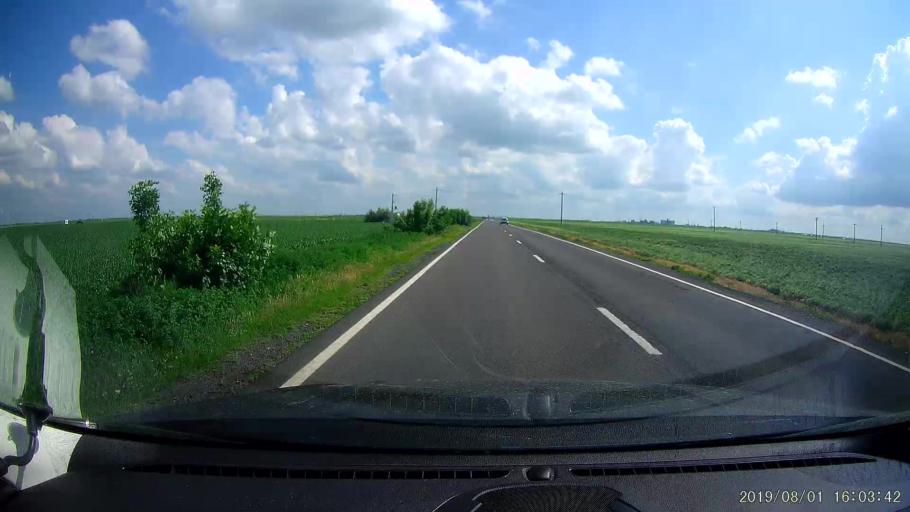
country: RO
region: Calarasi
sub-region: Comuna Dragalina
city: Drajna Noua
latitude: 44.4657
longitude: 27.3833
